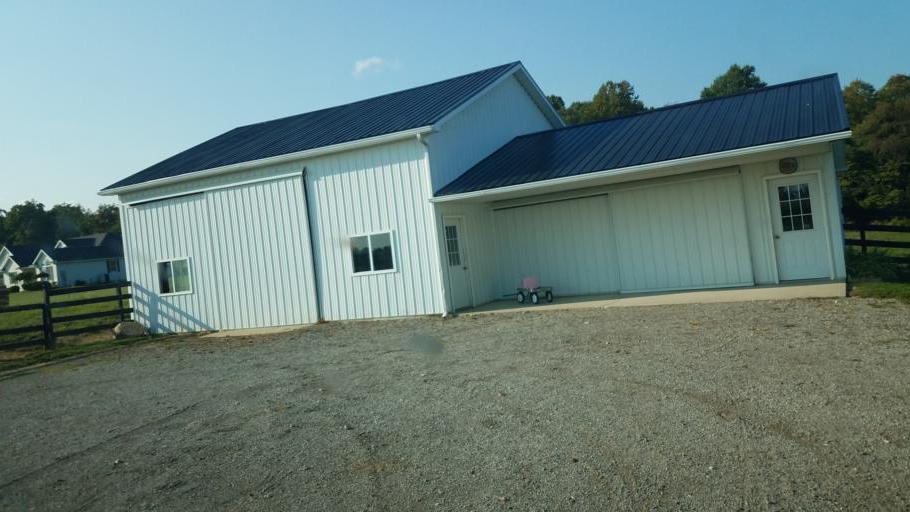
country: US
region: Ohio
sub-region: Knox County
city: Fredericktown
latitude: 40.5578
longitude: -82.5911
